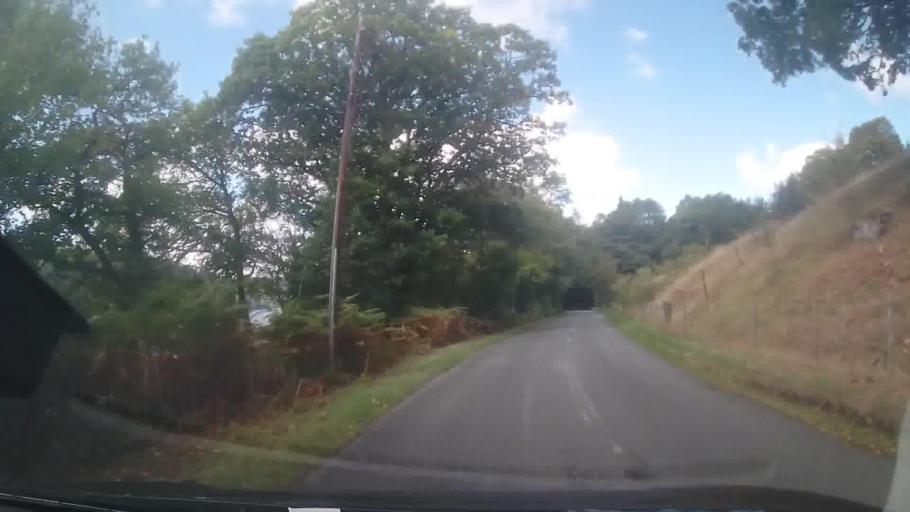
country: GB
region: Wales
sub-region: Sir Powys
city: Llangynog
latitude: 52.7774
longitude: -3.4777
